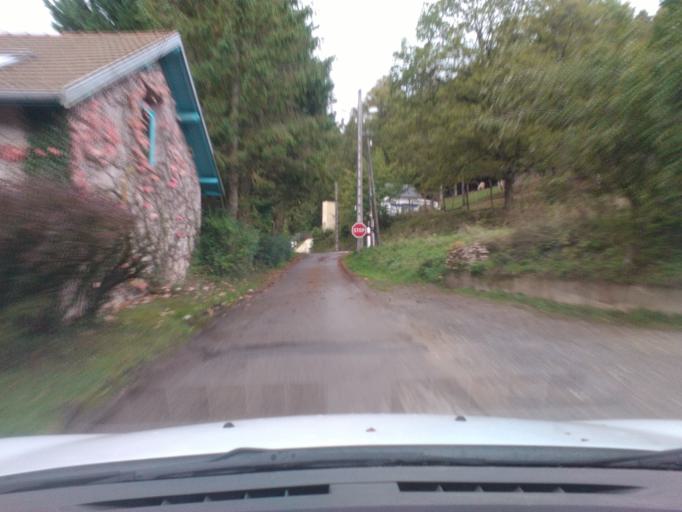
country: FR
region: Lorraine
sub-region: Departement des Vosges
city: Saint-Die-des-Vosges
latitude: 48.3210
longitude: 6.9791
